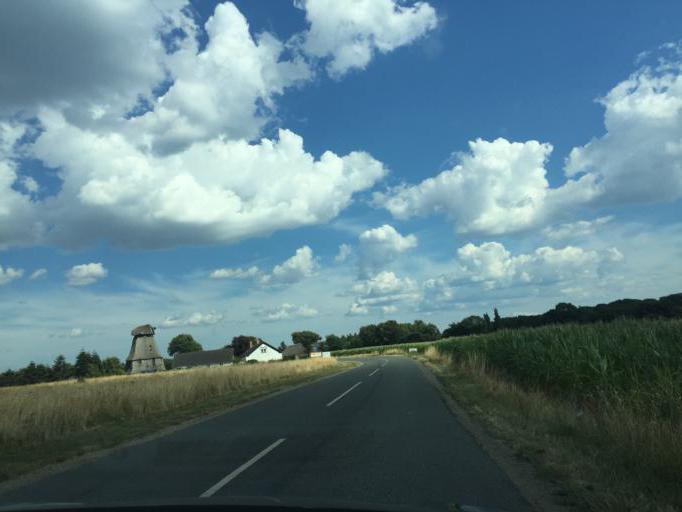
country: DK
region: South Denmark
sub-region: Assens Kommune
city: Harby
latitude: 55.1534
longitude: 10.0118
